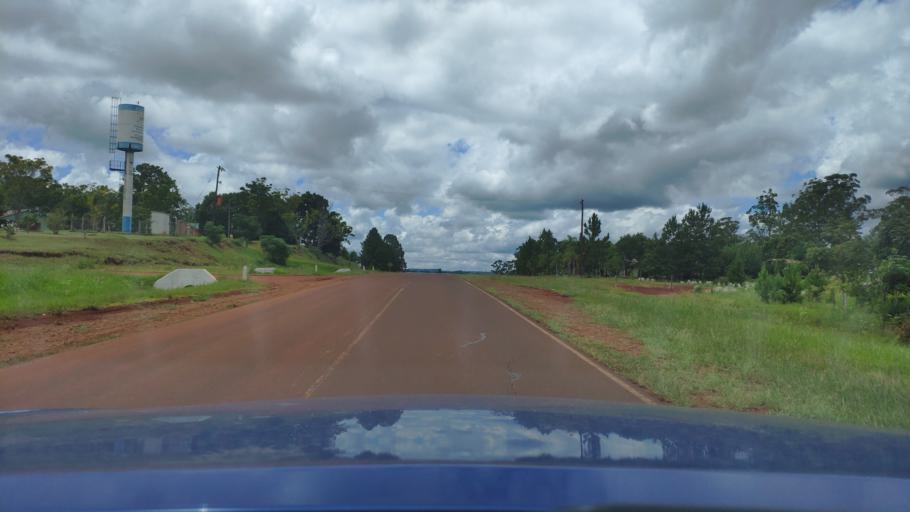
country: AR
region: Misiones
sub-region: Departamento de San Javier
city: San Javier
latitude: -27.8559
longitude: -55.2509
